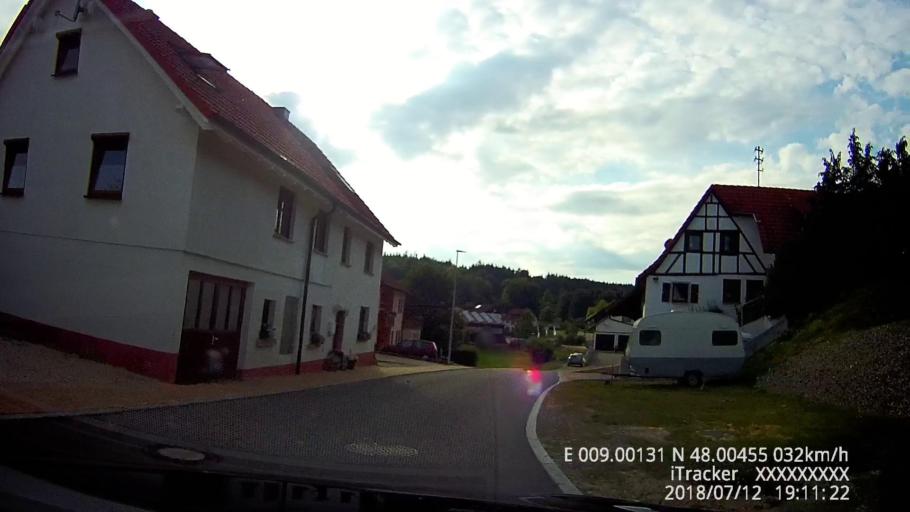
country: DE
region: Baden-Wuerttemberg
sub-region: Tuebingen Region
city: Leibertingen
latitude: 48.0457
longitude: 9.0129
